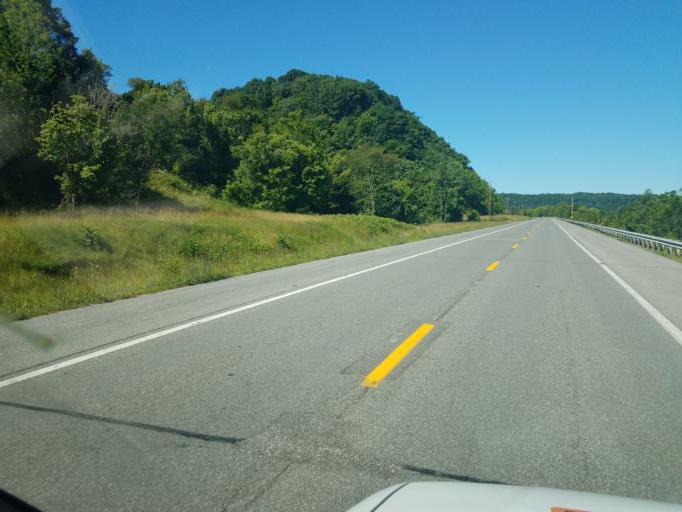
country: US
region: West Virginia
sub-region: Cabell County
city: Lesage
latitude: 38.5841
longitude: -82.2666
